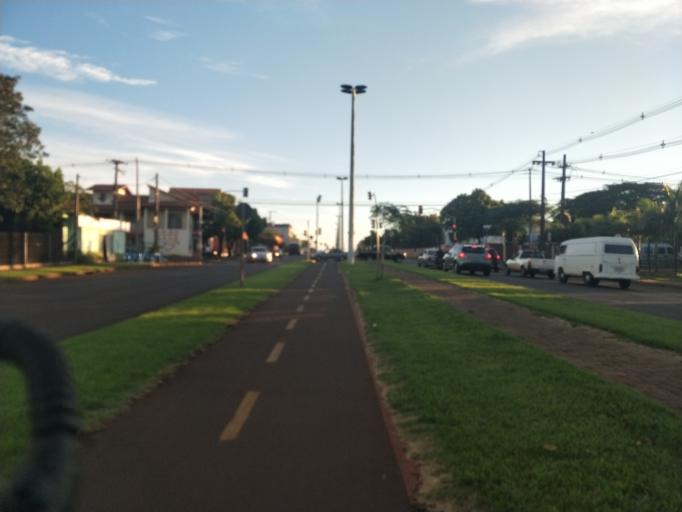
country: BR
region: Parana
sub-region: Marechal Candido Rondon
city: Marechal Candido Rondon
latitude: -24.5576
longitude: -54.0481
